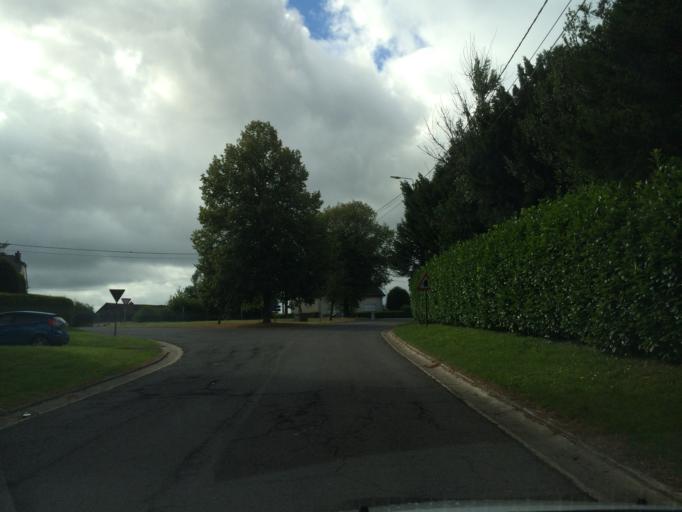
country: BE
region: Wallonia
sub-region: Province du Luxembourg
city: Chiny
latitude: 49.6979
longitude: 5.3735
